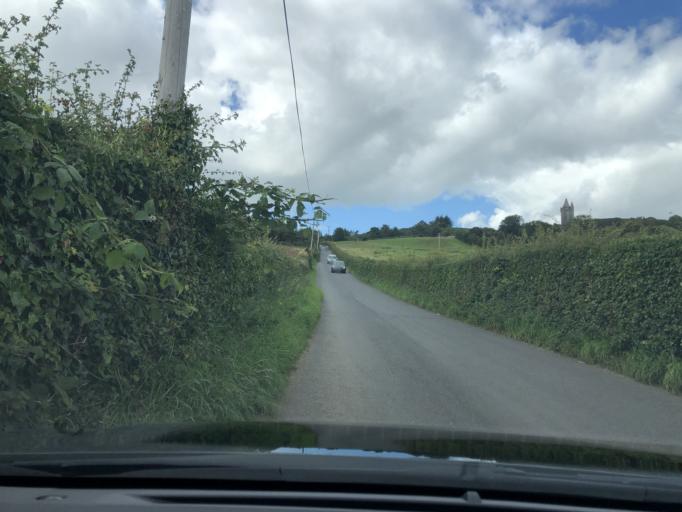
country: GB
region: Northern Ireland
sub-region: Ards District
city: Newtownards
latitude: 54.5746
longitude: -5.7165
